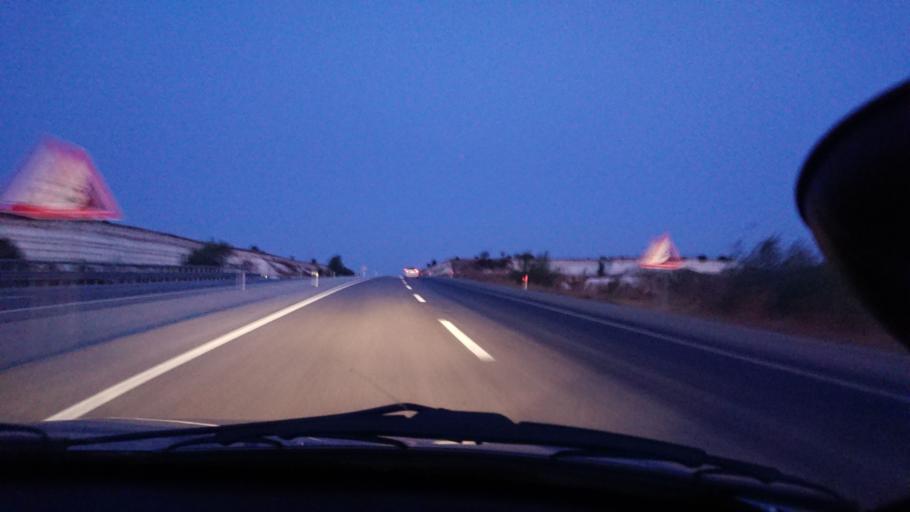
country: TR
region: Kuetahya
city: Cavdarhisar
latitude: 39.1400
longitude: 29.5662
